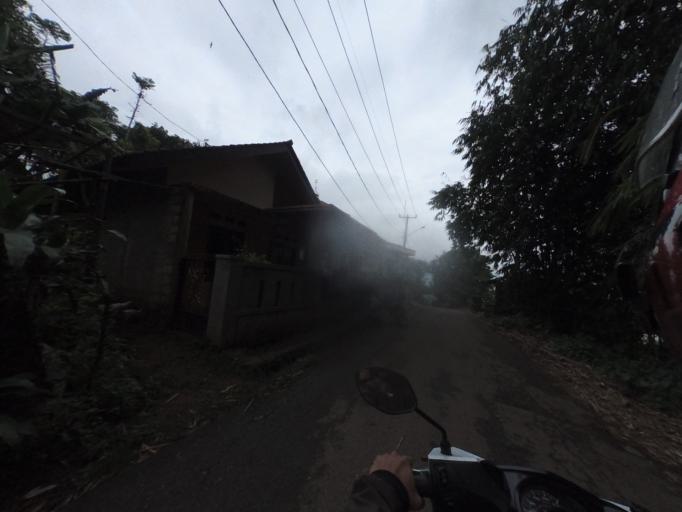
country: ID
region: West Java
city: Bogor
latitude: -6.6254
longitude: 106.7460
